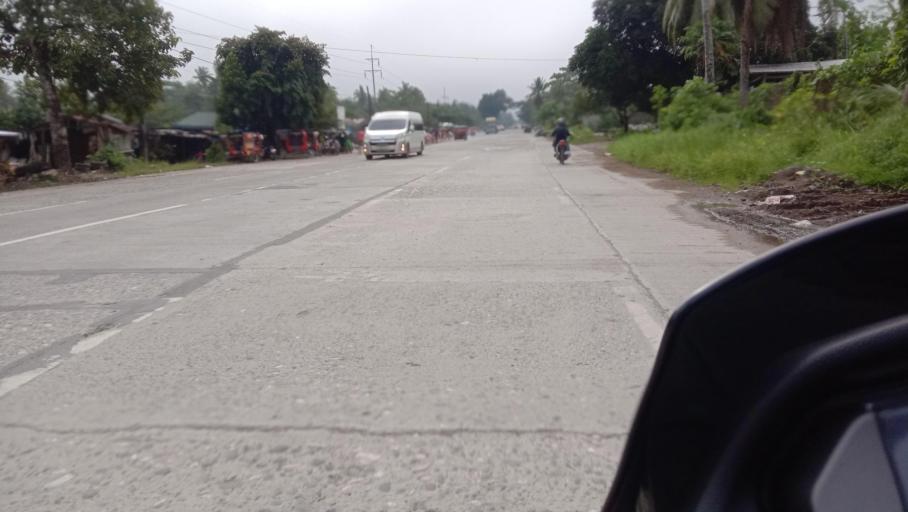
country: PH
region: Caraga
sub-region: Province of Agusan del Sur
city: Alegria
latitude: 8.5053
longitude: 125.9889
